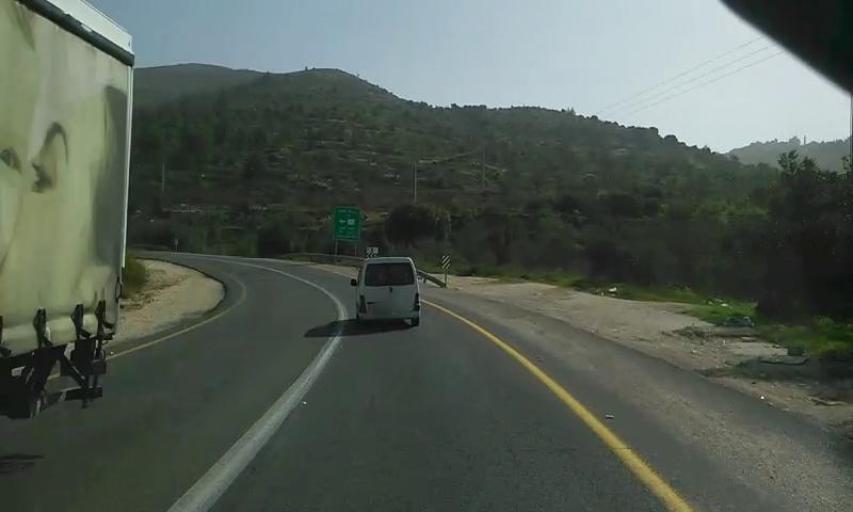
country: PS
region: West Bank
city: Silwad
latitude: 31.9950
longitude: 35.2491
